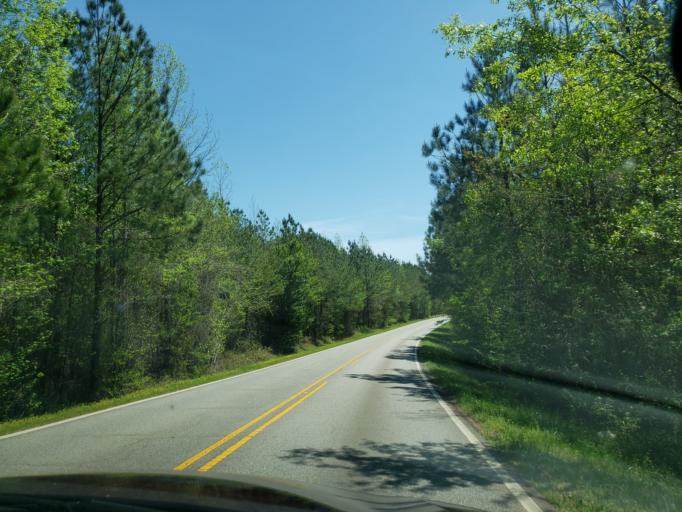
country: US
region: Alabama
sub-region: Tallapoosa County
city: Camp Hill
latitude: 32.7031
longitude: -85.7072
